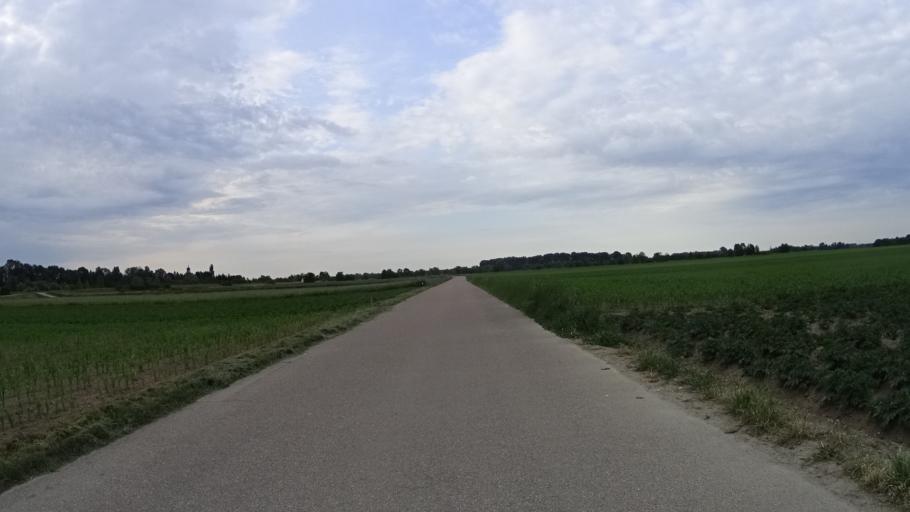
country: DE
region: Bavaria
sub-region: Lower Bavaria
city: Kirchroth
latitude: 48.9356
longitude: 12.5411
